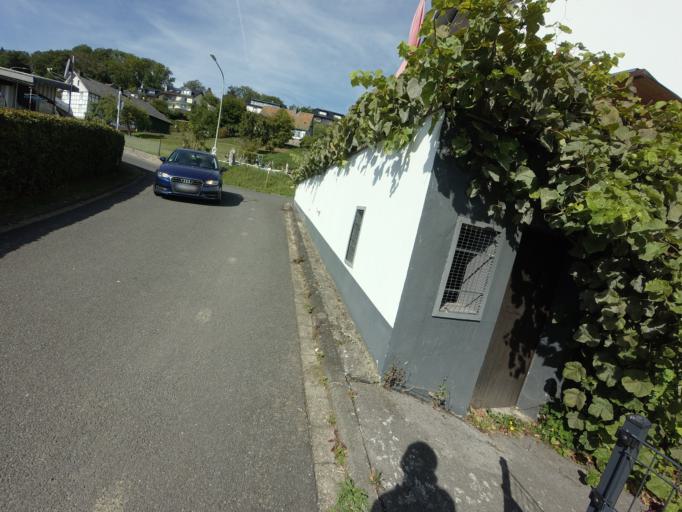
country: DE
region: North Rhine-Westphalia
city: Heimbach
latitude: 50.6302
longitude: 6.3870
